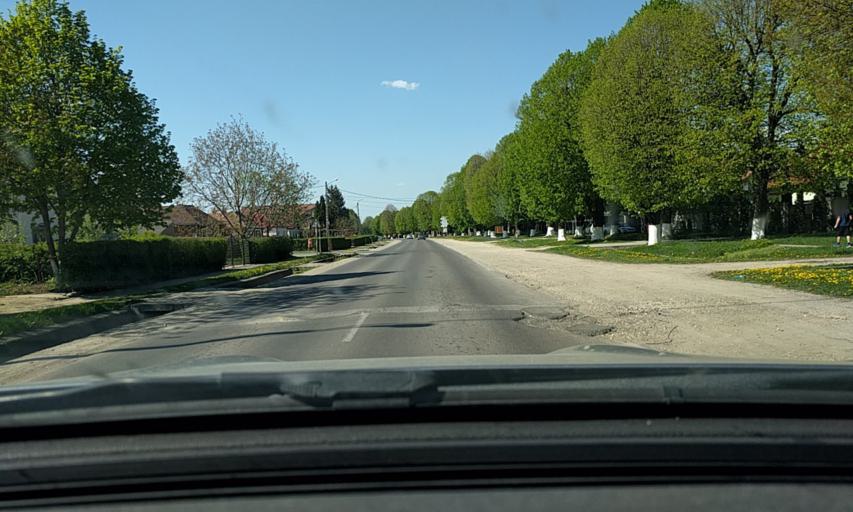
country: RO
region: Brasov
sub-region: Comuna Harman
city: Harman
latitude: 45.7063
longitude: 25.6875
